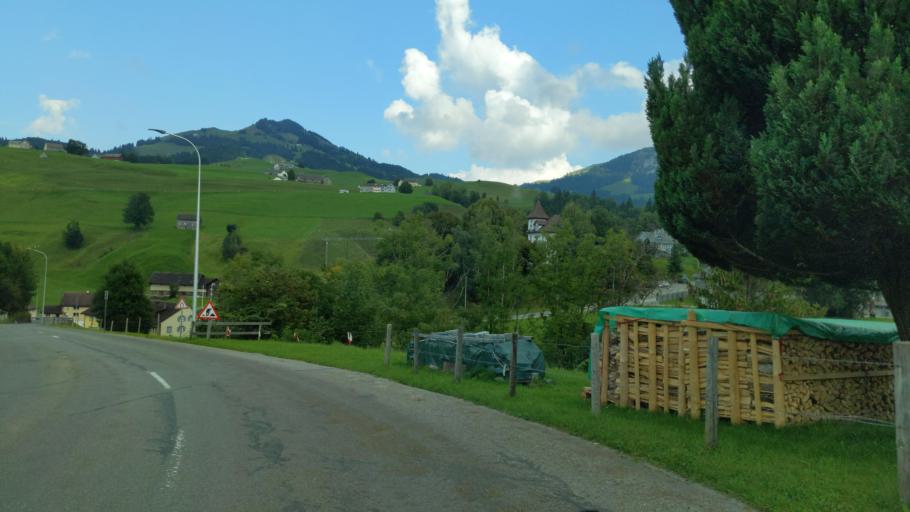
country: CH
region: Appenzell Innerrhoden
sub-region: Appenzell Inner Rhodes
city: Appenzell
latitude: 47.3071
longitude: 9.4335
